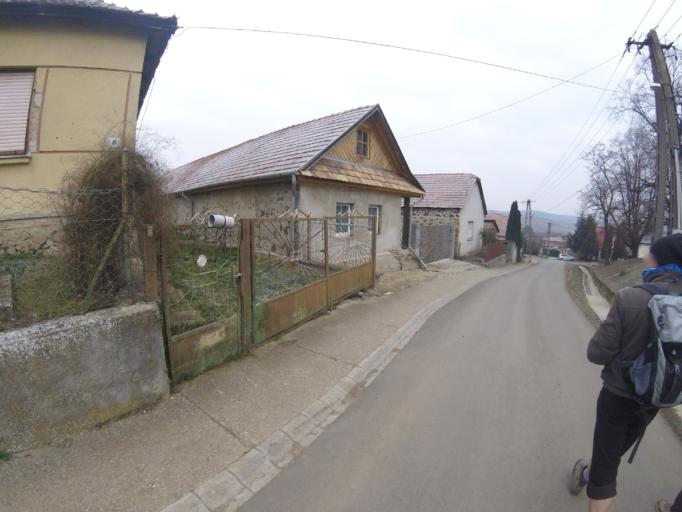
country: HU
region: Nograd
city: Paszto
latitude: 47.9586
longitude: 19.6824
